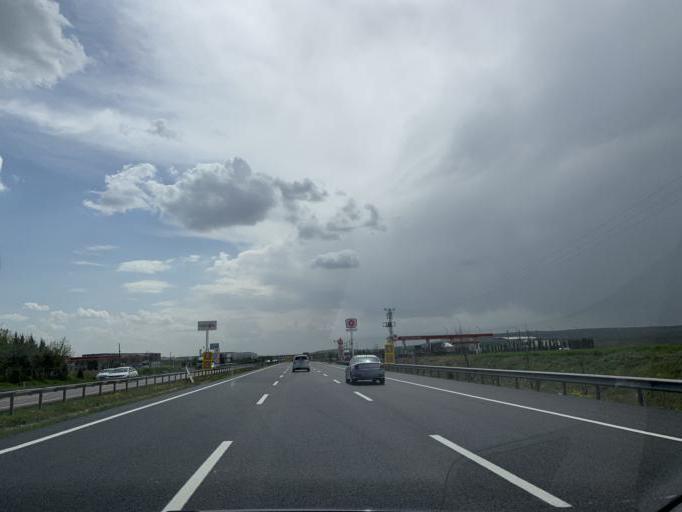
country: TR
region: Ankara
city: Polatli
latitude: 39.6576
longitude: 32.2193
